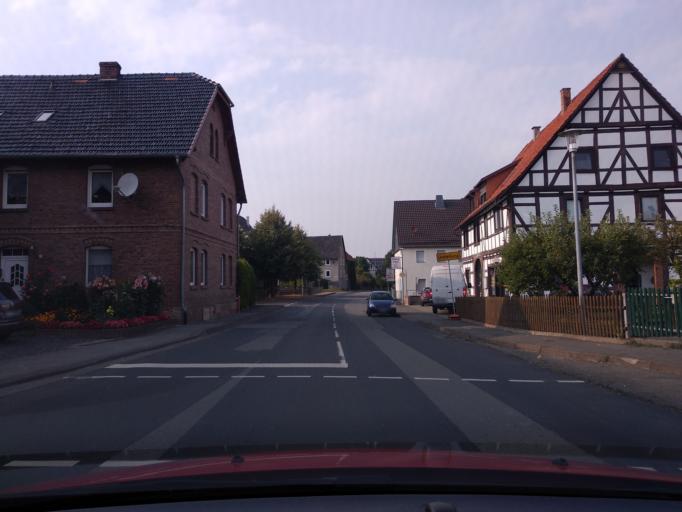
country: DE
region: Hesse
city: Liebenau
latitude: 51.4586
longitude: 9.3074
